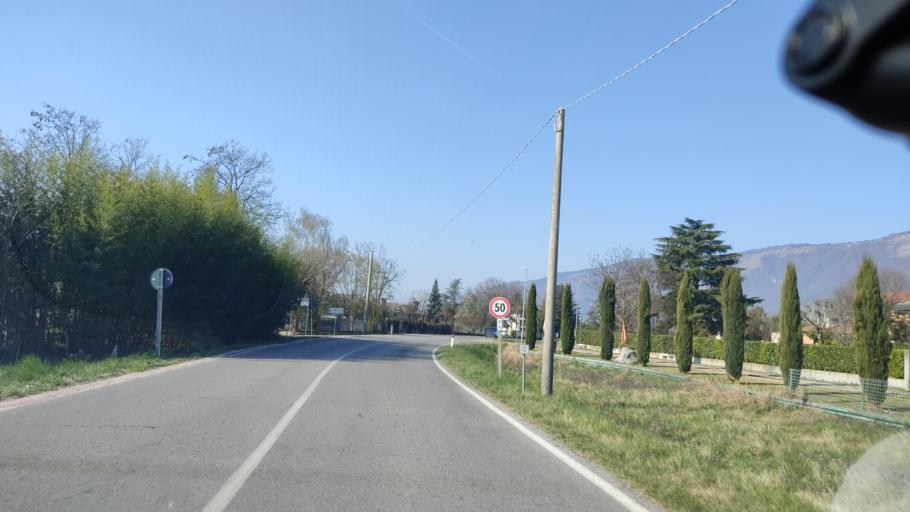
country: IT
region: Friuli Venezia Giulia
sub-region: Provincia di Pordenone
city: Budoia
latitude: 46.0518
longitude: 12.5406
